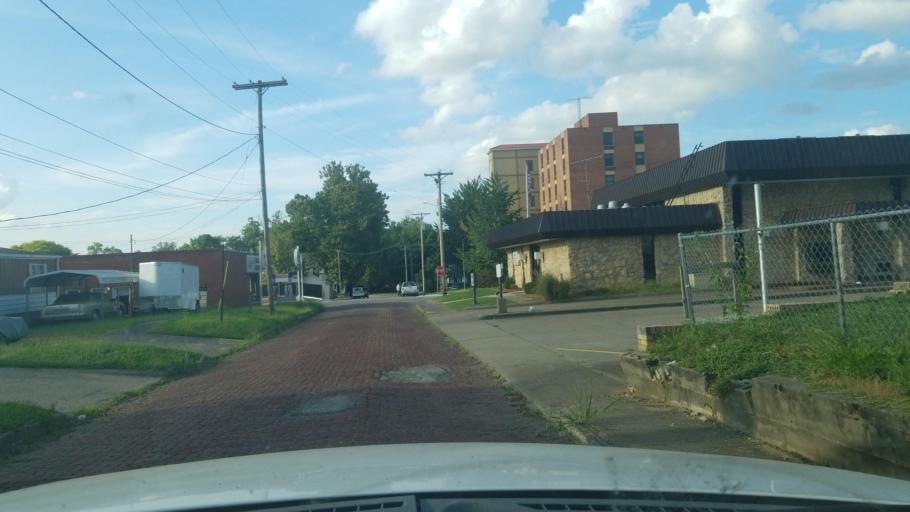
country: US
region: Illinois
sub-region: Saline County
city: Harrisburg
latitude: 37.7365
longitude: -88.5362
